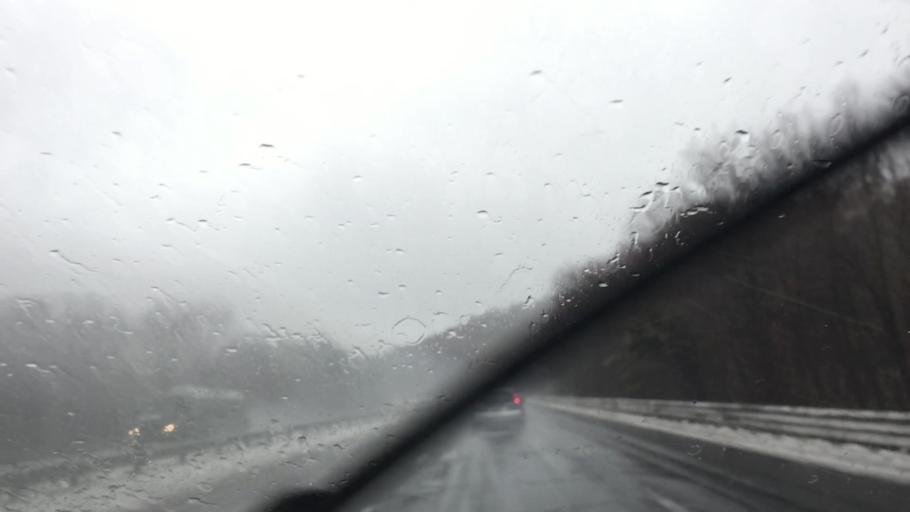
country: US
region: Massachusetts
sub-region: Hampden County
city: Granville
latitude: 42.1706
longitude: -72.8774
